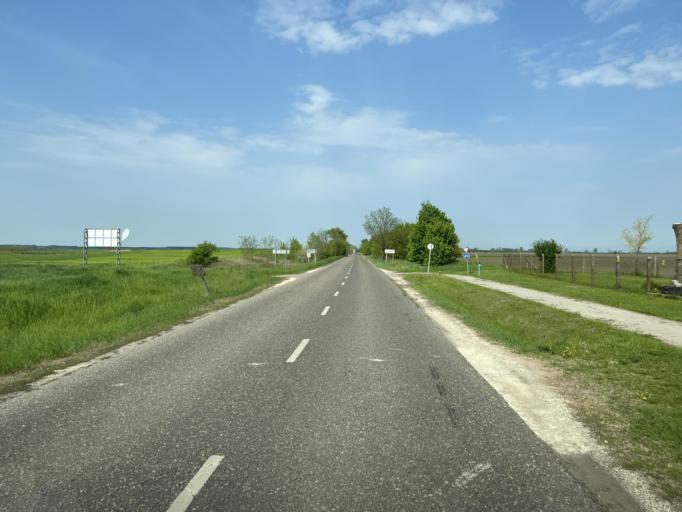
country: HU
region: Pest
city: Jaszkarajeno
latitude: 47.1002
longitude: 20.0158
